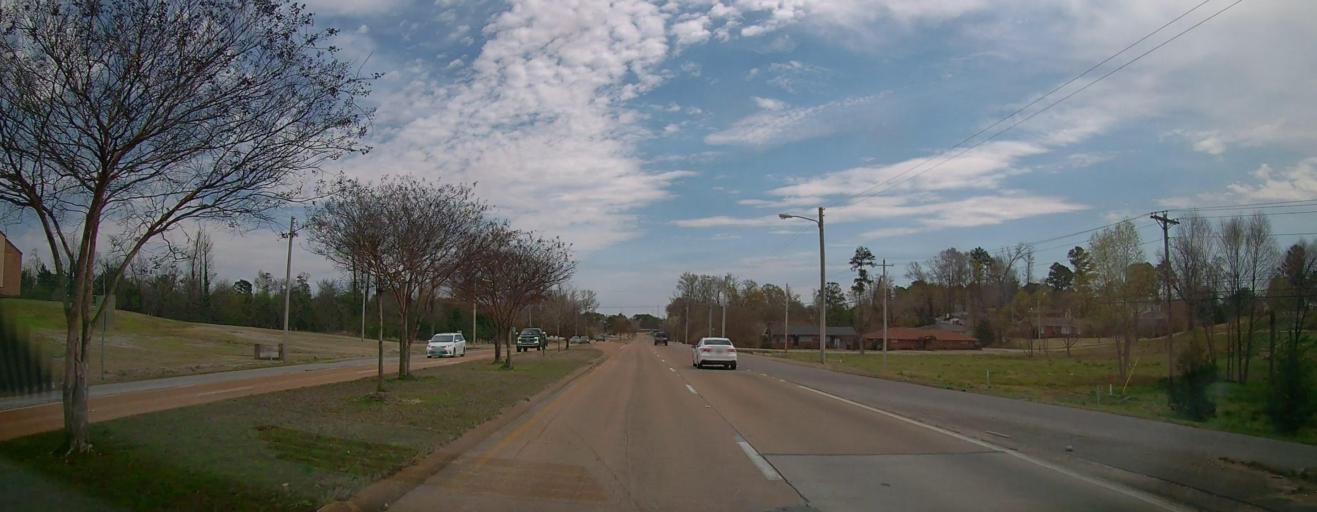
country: US
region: Mississippi
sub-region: Lee County
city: Tupelo
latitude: 34.2776
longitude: -88.7239
